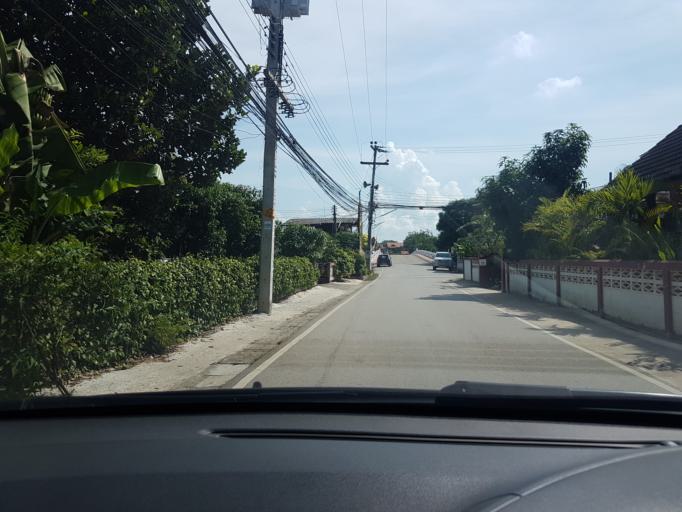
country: TH
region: Lampang
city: Ko Kha
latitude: 18.2188
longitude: 99.4138
